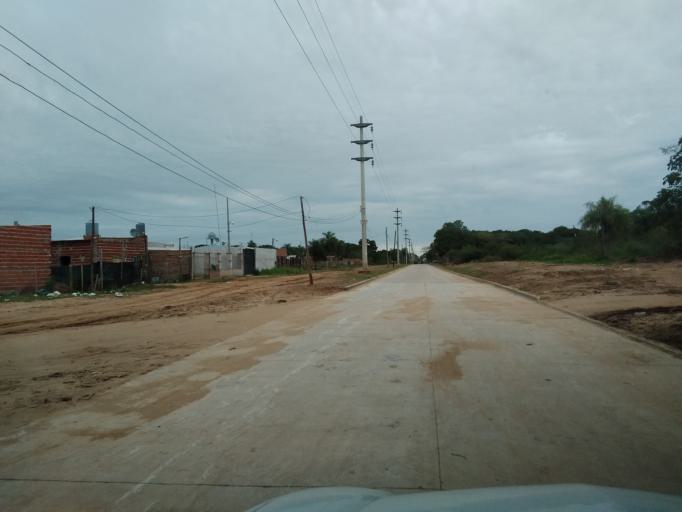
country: AR
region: Corrientes
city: Corrientes
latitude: -27.5110
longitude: -58.8219
